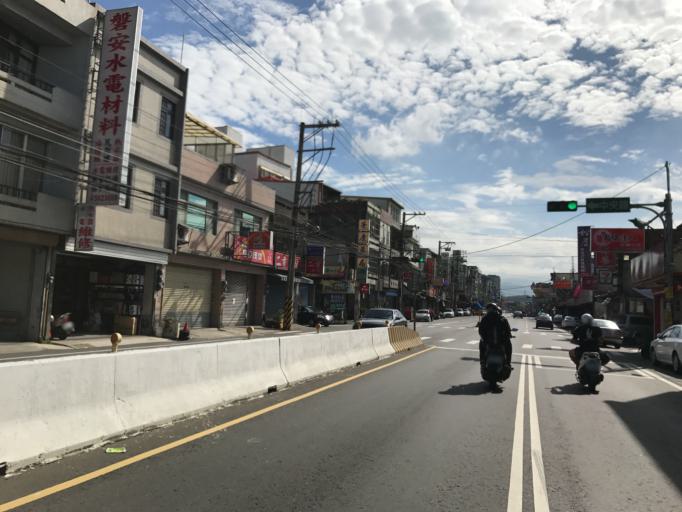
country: TW
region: Taiwan
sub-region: Hsinchu
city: Zhubei
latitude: 24.7684
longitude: 121.0551
